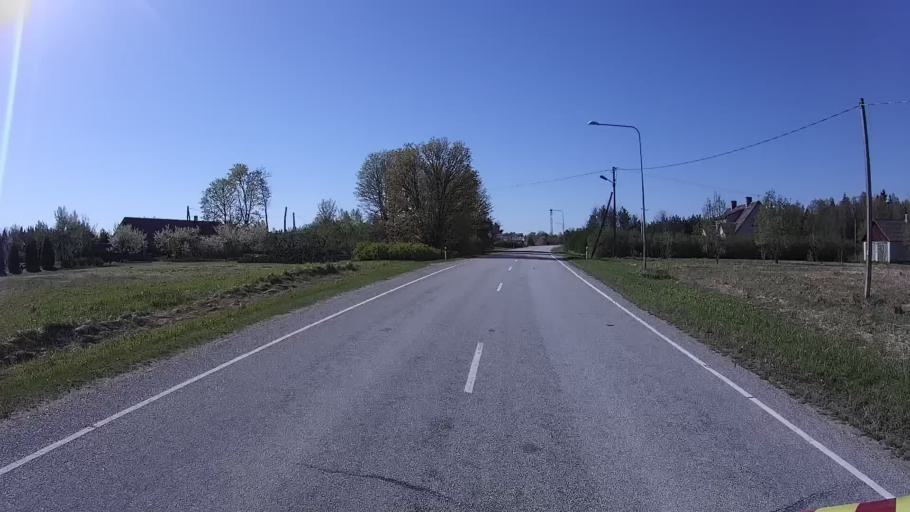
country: EE
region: Raplamaa
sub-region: Jaervakandi vald
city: Jarvakandi
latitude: 58.7924
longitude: 24.8189
